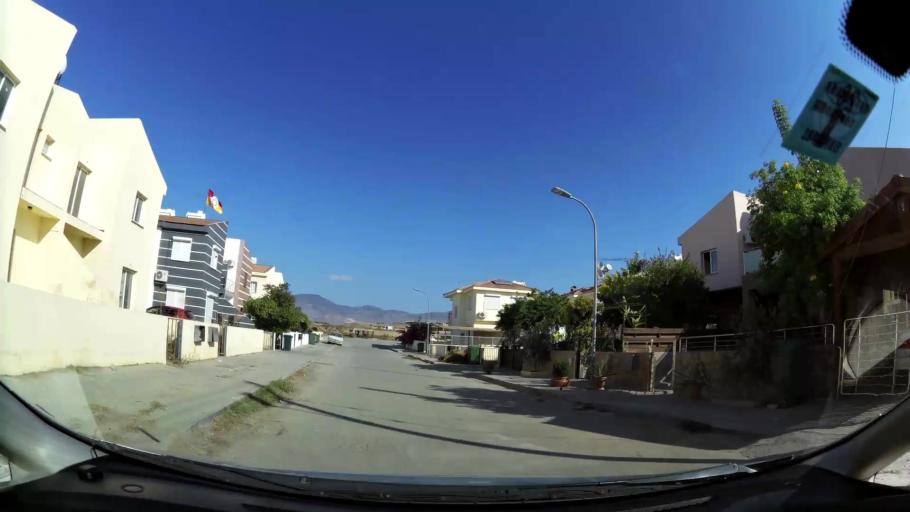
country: CY
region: Lefkosia
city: Nicosia
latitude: 35.2152
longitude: 33.3670
